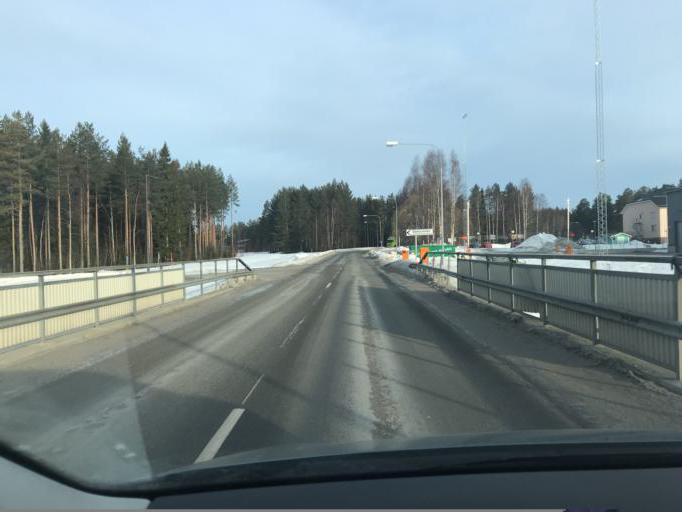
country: SE
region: Norrbotten
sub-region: Lulea Kommun
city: Bergnaset
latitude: 65.6163
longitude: 22.1225
